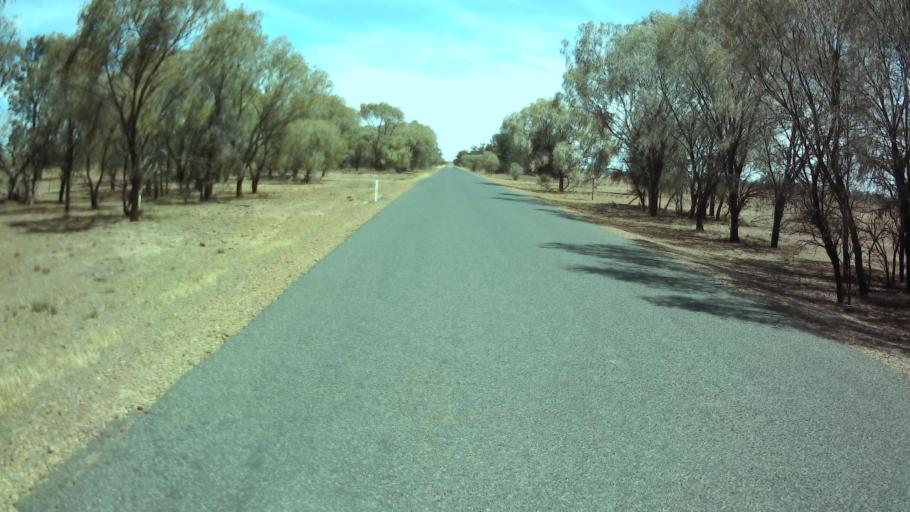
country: AU
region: New South Wales
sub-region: Weddin
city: Grenfell
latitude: -33.8756
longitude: 147.7439
